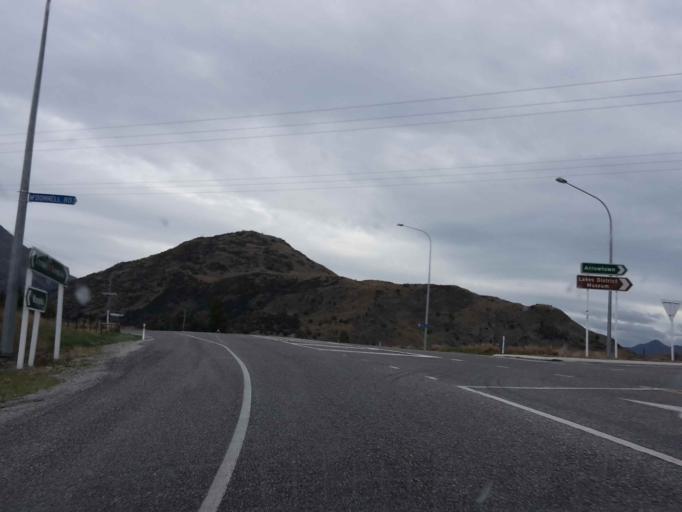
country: NZ
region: Otago
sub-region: Queenstown-Lakes District
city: Arrowtown
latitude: -44.9775
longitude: 168.8495
